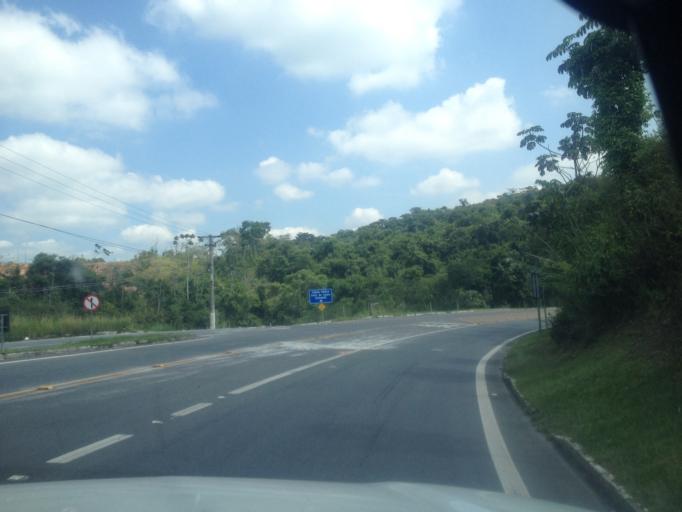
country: BR
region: Rio de Janeiro
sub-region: Volta Redonda
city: Volta Redonda
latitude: -22.5912
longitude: -44.0830
